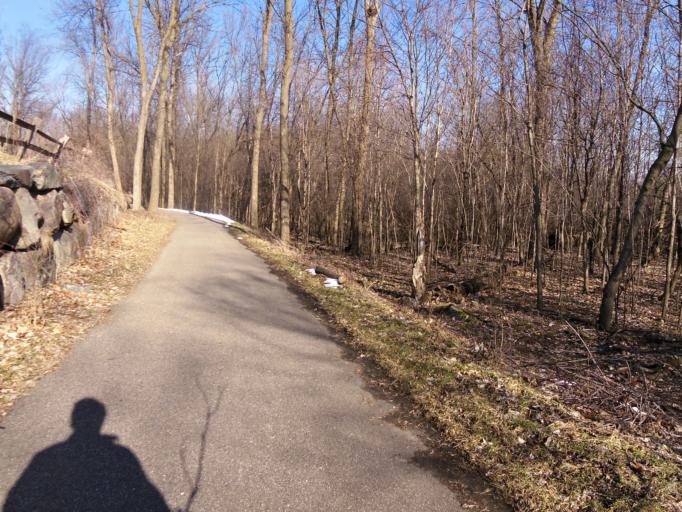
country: US
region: Minnesota
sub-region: Scott County
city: Prior Lake
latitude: 44.6988
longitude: -93.4405
